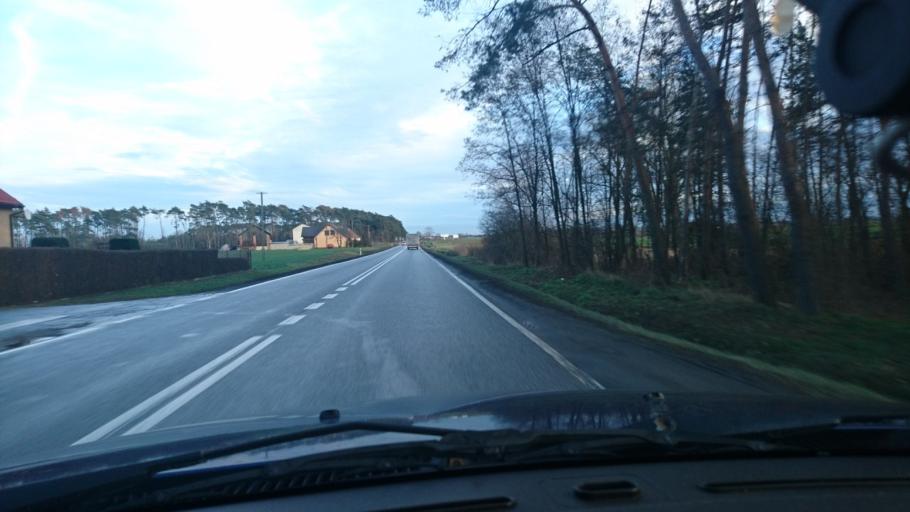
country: PL
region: Greater Poland Voivodeship
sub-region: Powiat kepinski
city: Leka Opatowska
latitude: 51.2233
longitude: 18.1165
